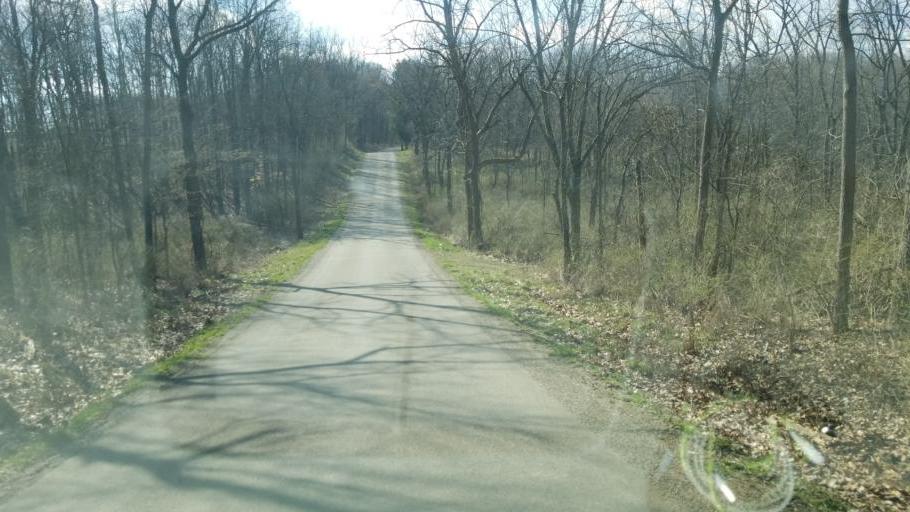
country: US
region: Ohio
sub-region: Licking County
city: Utica
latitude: 40.2616
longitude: -82.3132
